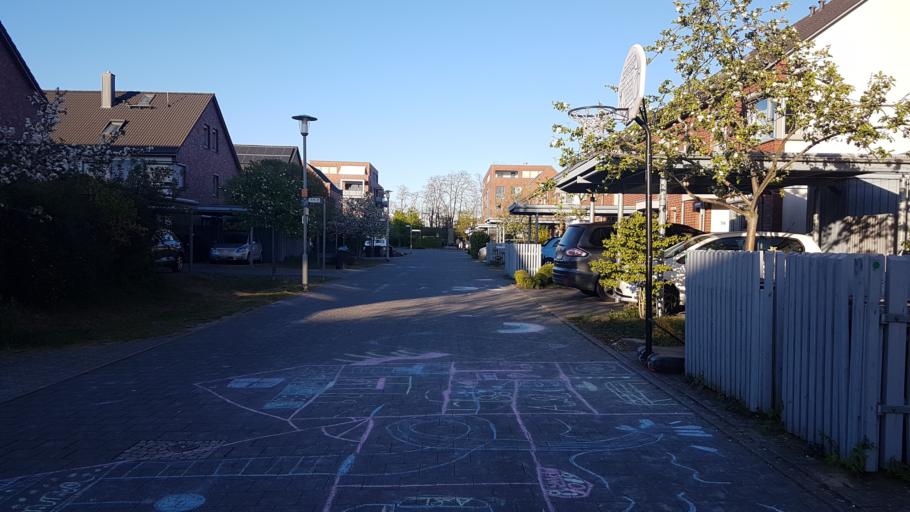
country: DE
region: Lower Saxony
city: Hannover
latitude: 52.4042
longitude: 9.7882
